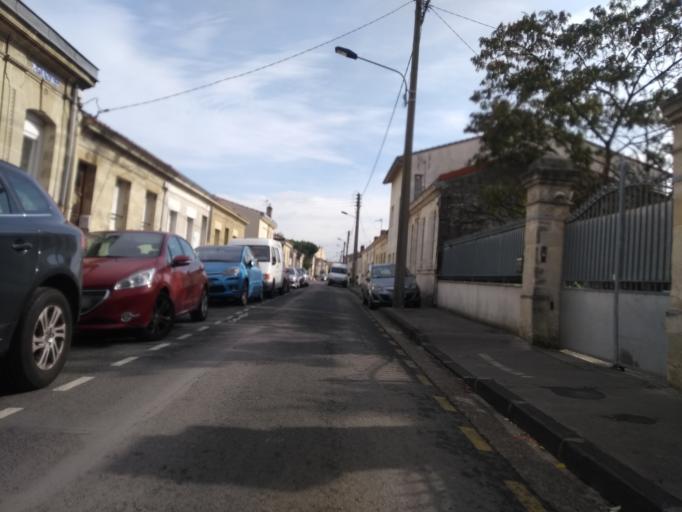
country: FR
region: Aquitaine
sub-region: Departement de la Gironde
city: Talence
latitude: 44.8229
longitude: -0.5976
